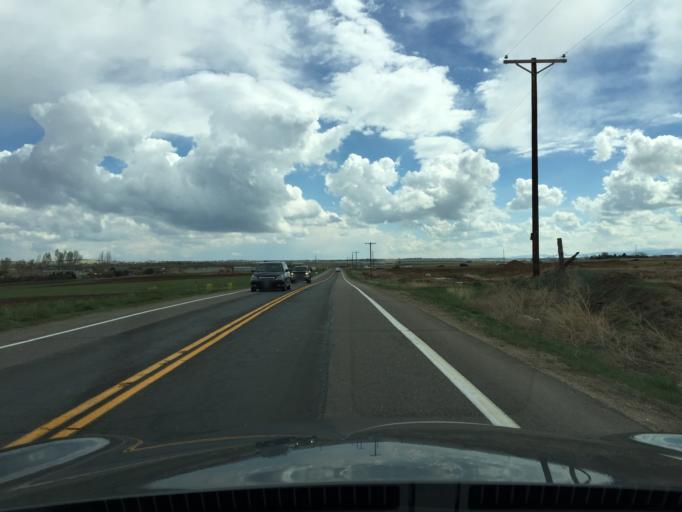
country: US
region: Colorado
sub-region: Boulder County
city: Erie
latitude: 40.0178
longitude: -105.0554
